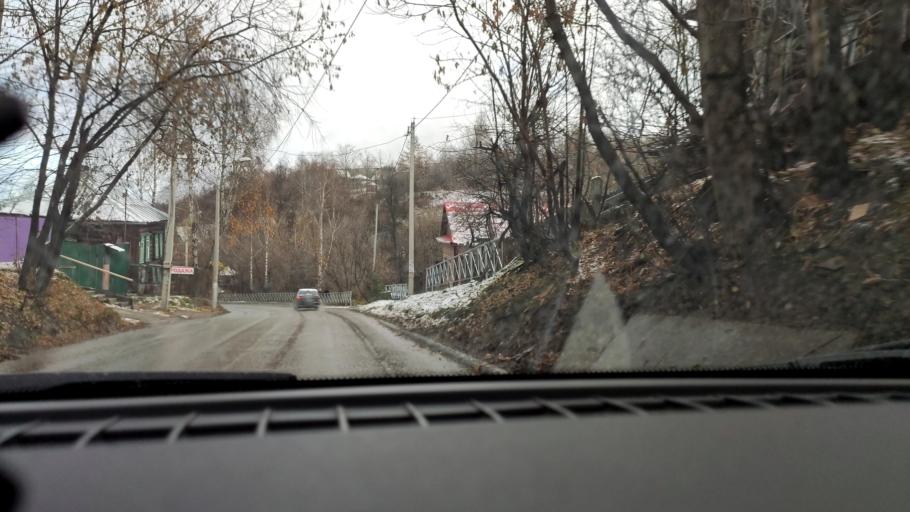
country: RU
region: Perm
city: Perm
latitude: 58.0267
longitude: 56.3145
